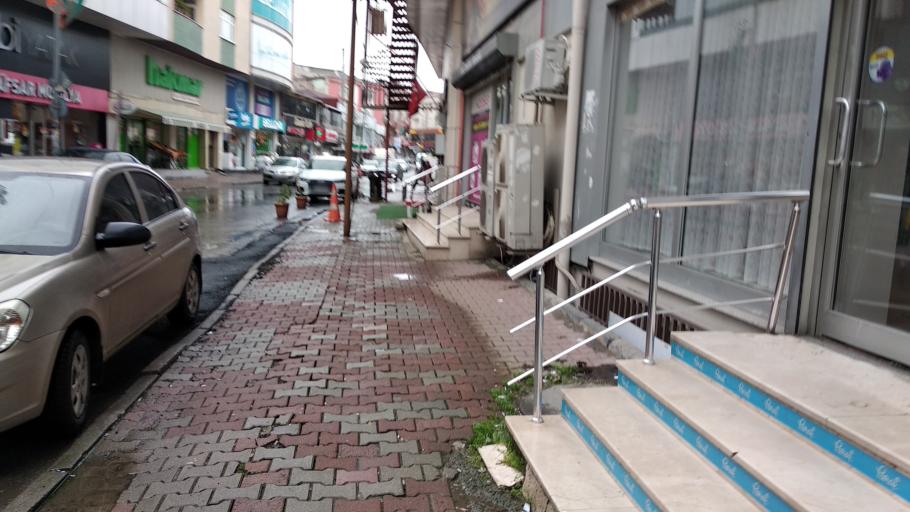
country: TR
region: Istanbul
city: Samandira
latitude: 41.0168
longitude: 29.1907
